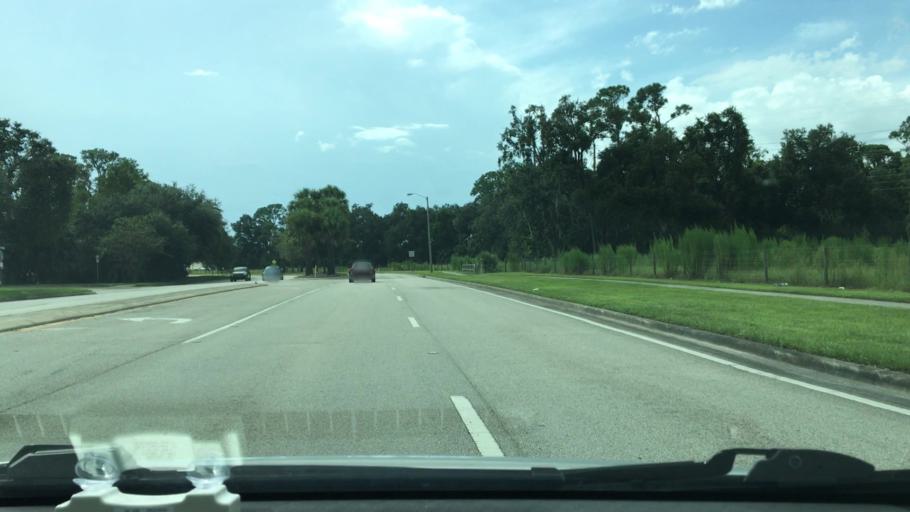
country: US
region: Florida
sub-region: Seminole County
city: Lake Mary
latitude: 28.8046
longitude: -81.3283
